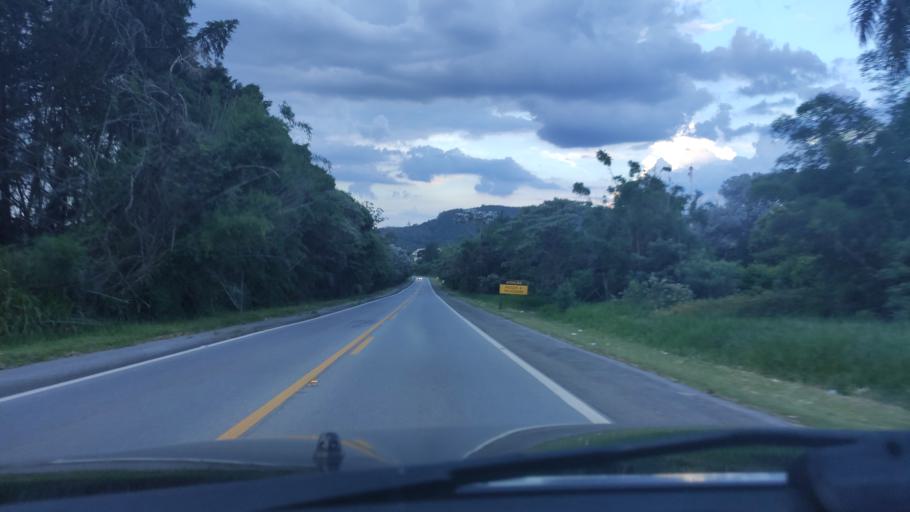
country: BR
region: Sao Paulo
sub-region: Braganca Paulista
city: Braganca Paulista
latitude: -22.8791
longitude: -46.5357
